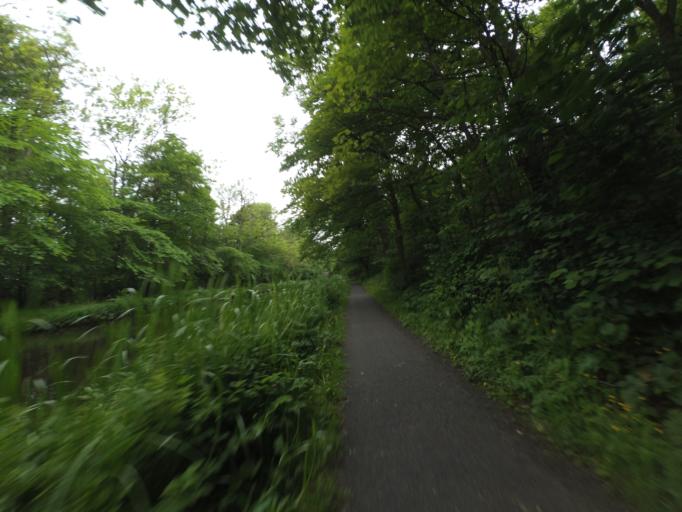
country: GB
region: Scotland
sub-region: West Lothian
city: Broxburn
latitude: 55.9689
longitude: -3.4706
